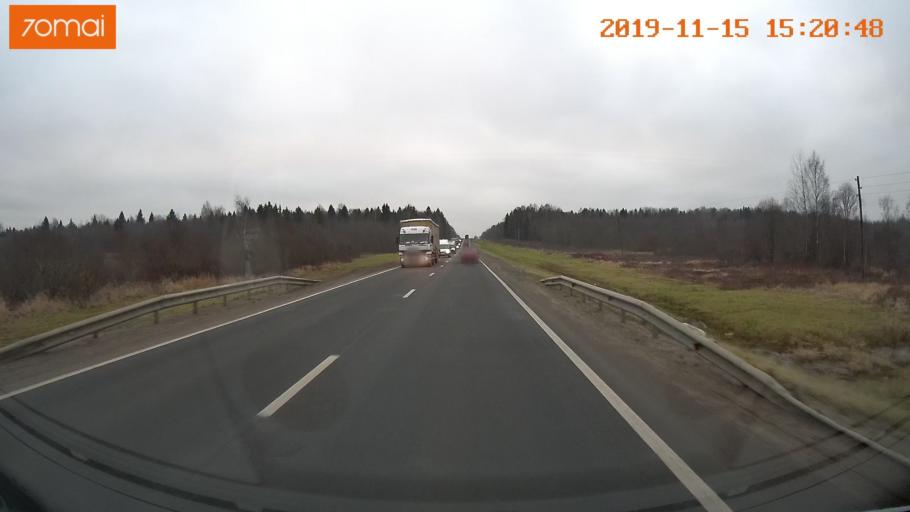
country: RU
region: Jaroslavl
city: Danilov
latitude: 58.2196
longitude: 40.1560
